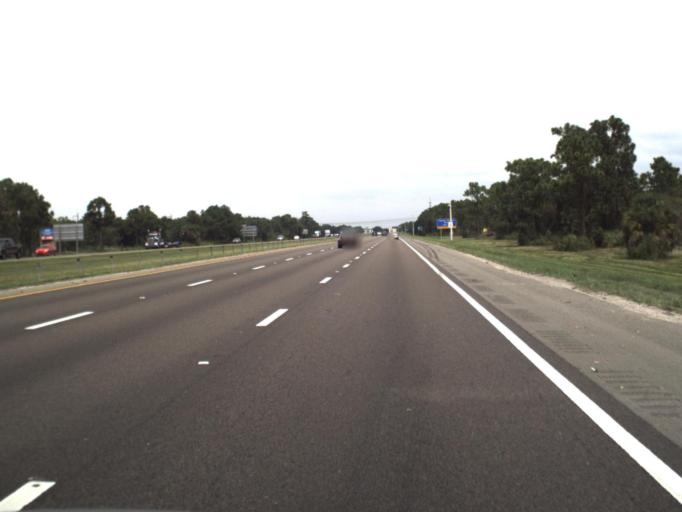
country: US
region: Florida
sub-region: Sarasota County
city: The Meadows
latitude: 27.3979
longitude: -82.4511
